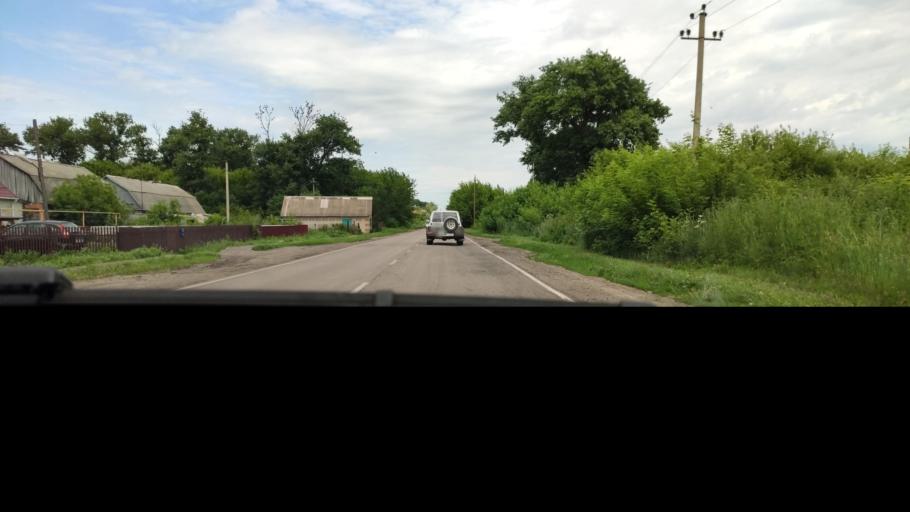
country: RU
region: Voronezj
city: Panino
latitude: 51.6558
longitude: 40.1215
